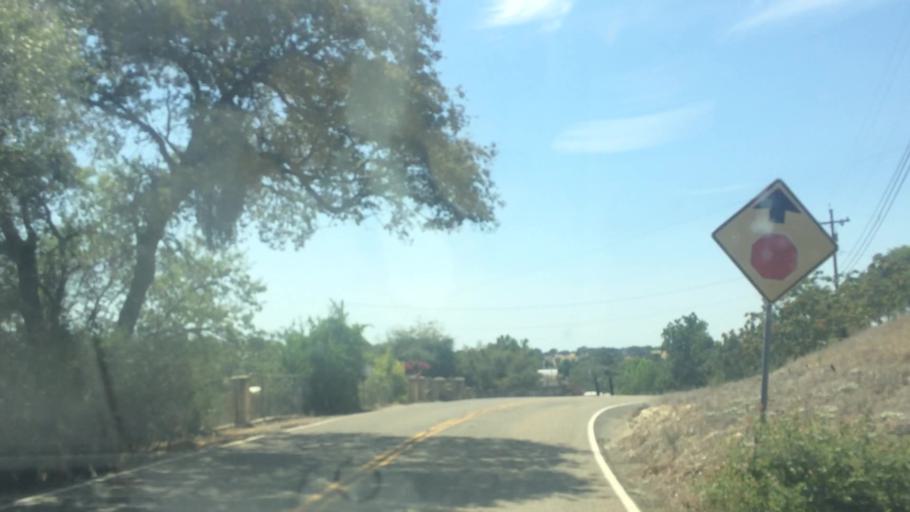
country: US
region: California
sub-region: Amador County
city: Sutter Creek
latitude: 38.3820
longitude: -120.7977
